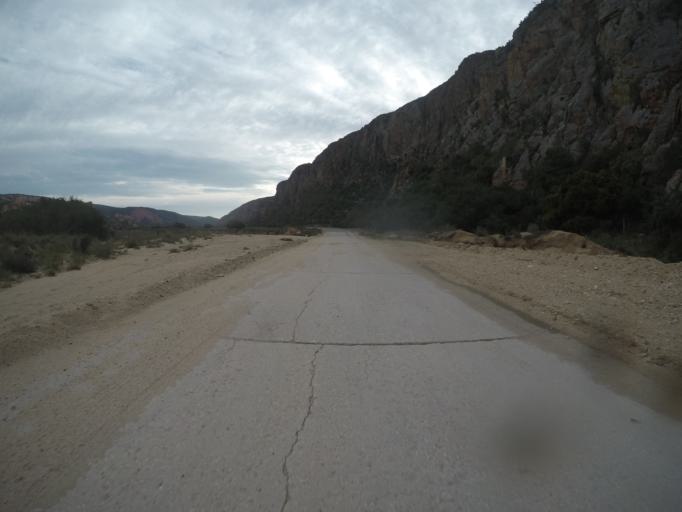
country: ZA
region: Eastern Cape
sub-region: Cacadu District Municipality
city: Willowmore
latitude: -33.5195
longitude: 23.6732
